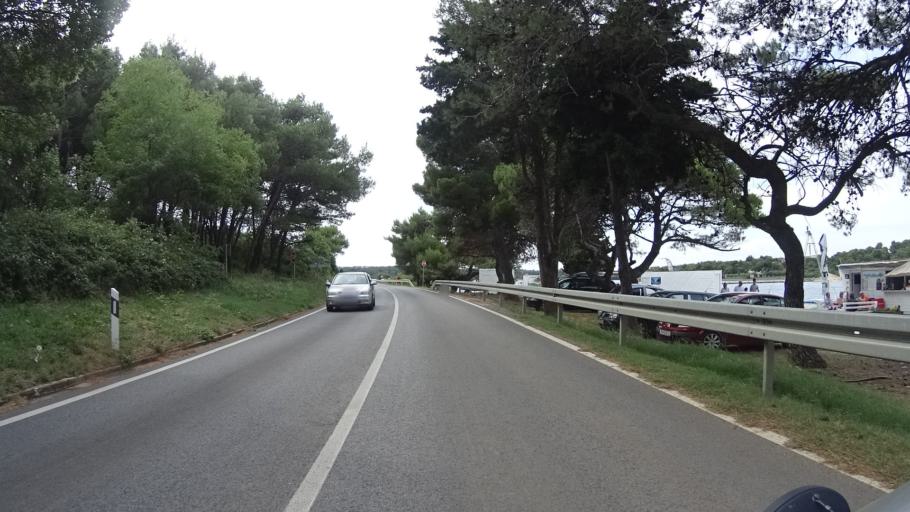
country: HR
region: Istarska
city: Medulin
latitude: 44.8163
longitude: 13.8984
